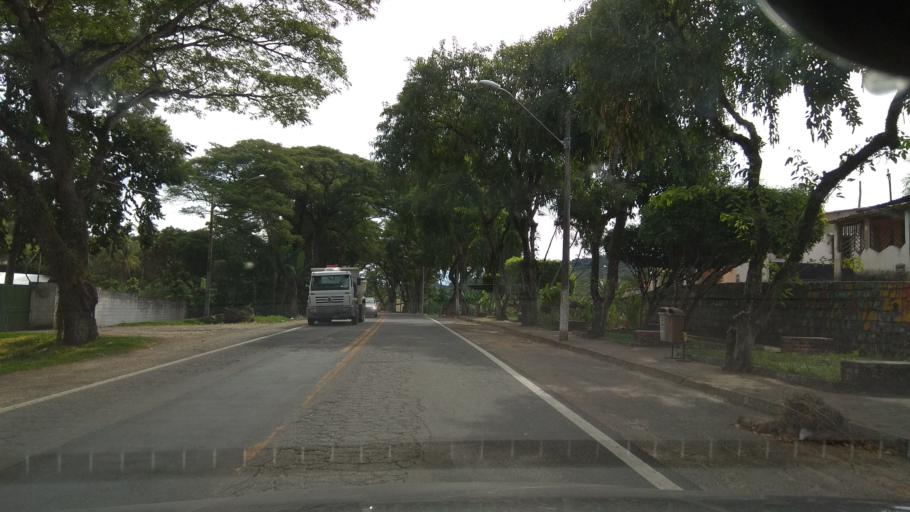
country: BR
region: Bahia
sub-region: Ubata
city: Ubata
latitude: -14.1994
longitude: -39.5361
